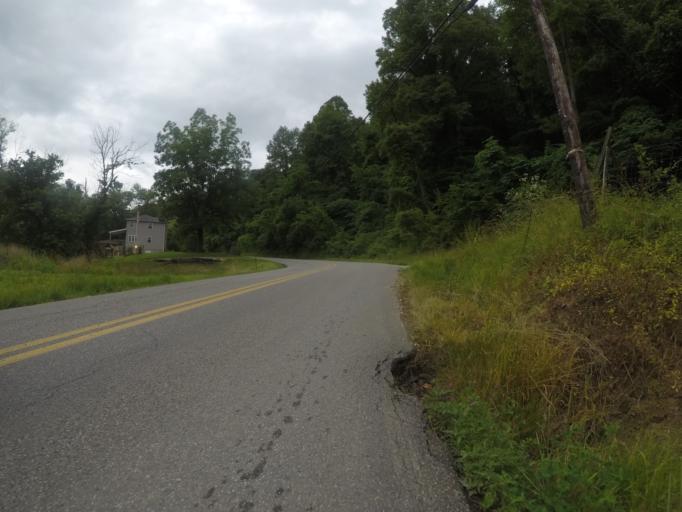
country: US
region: West Virginia
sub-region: Wayne County
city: Lavalette
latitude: 38.3637
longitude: -82.4251
